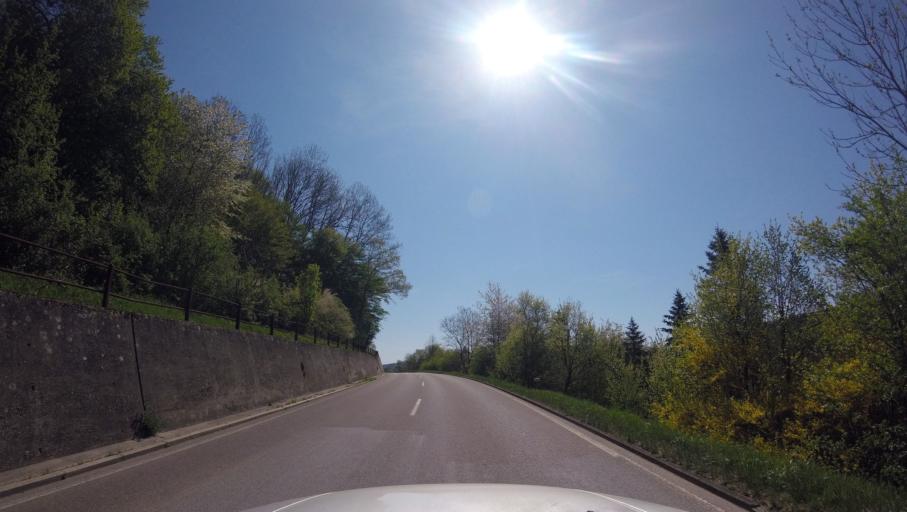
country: DE
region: Baden-Wuerttemberg
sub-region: Regierungsbezirk Stuttgart
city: Lorch
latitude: 48.7960
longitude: 9.7191
